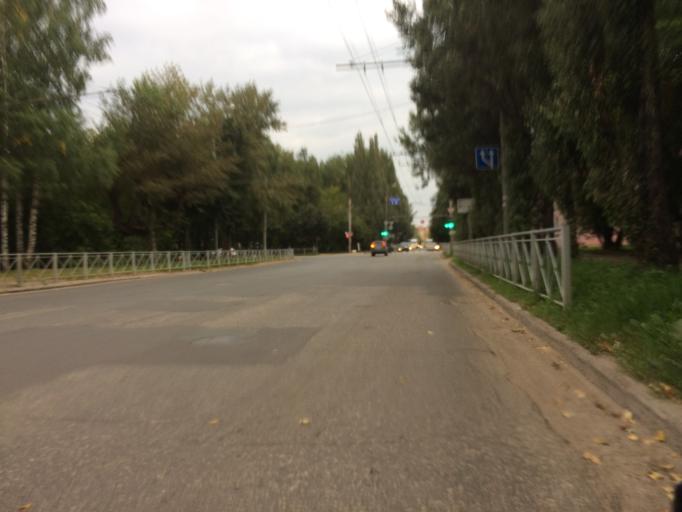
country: RU
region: Mariy-El
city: Yoshkar-Ola
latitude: 56.6360
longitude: 47.8651
